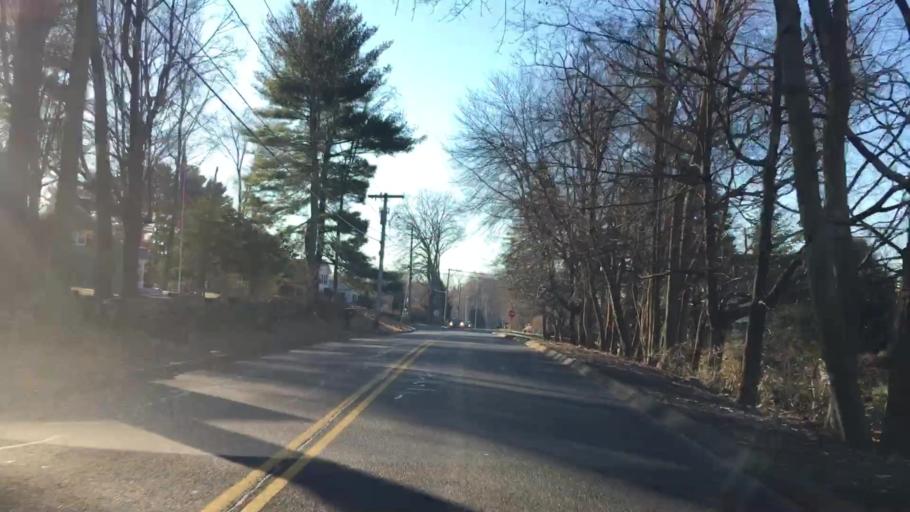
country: US
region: Connecticut
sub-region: New Haven County
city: Cheshire Village
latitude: 41.5500
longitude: -72.8680
